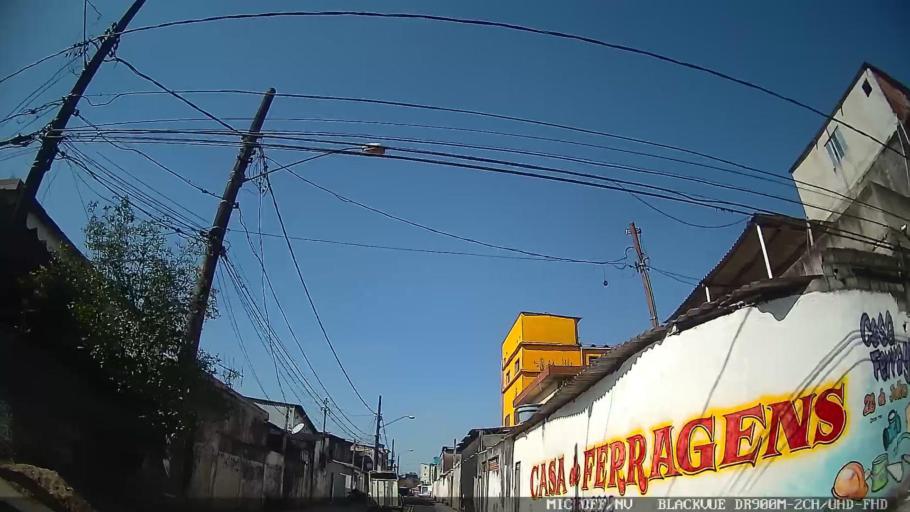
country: BR
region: Sao Paulo
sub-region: Santos
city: Santos
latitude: -23.9466
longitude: -46.2971
